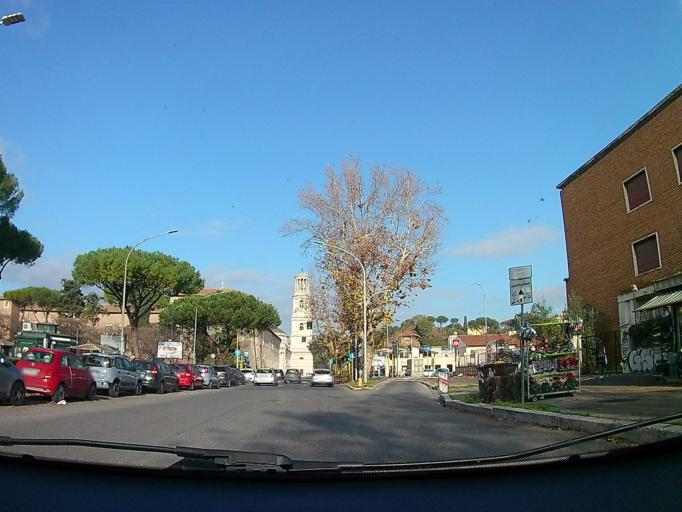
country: IT
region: Latium
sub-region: Citta metropolitana di Roma Capitale
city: Rome
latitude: 41.8563
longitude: 12.4773
